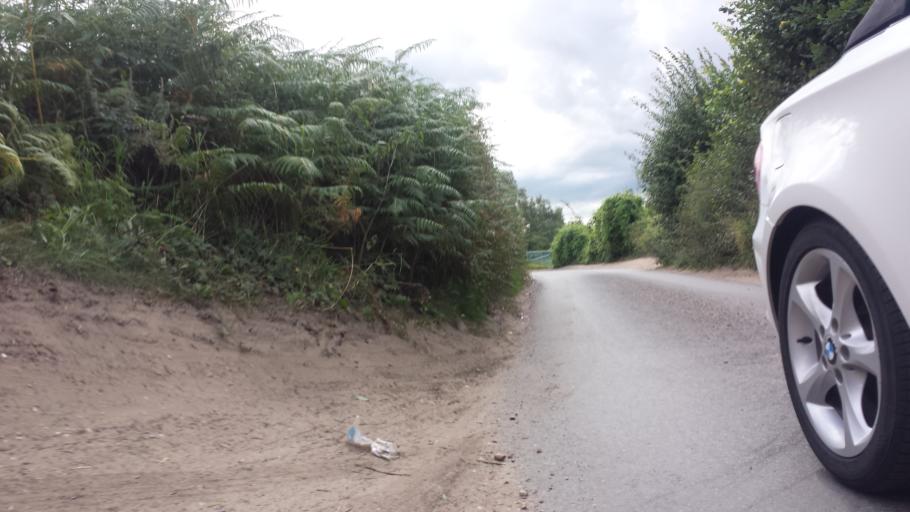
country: GB
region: England
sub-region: Kent
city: Swanley
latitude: 51.4010
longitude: 0.1935
